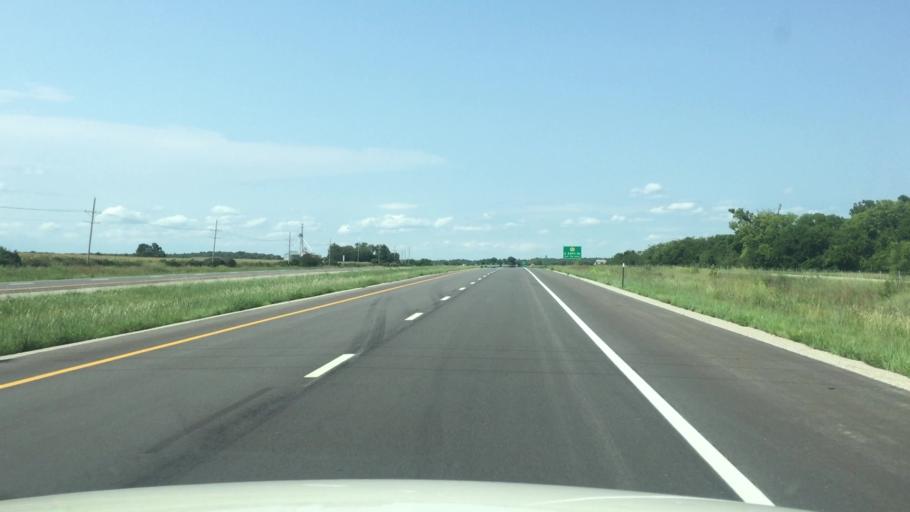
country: US
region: Kansas
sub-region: Linn County
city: La Cygne
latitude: 38.3236
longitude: -94.6774
